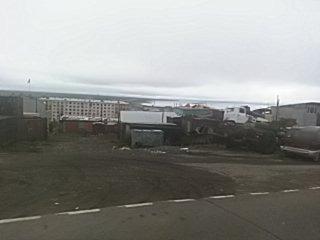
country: RU
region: Krasnoyarskiy
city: Dudinka
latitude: 69.4097
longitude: 86.1917
